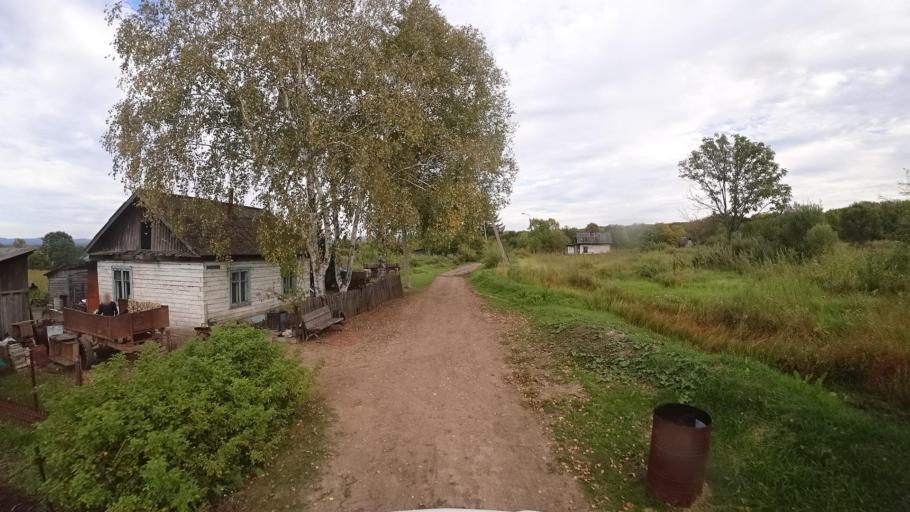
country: RU
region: Primorskiy
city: Dostoyevka
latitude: 44.3457
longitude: 133.4072
